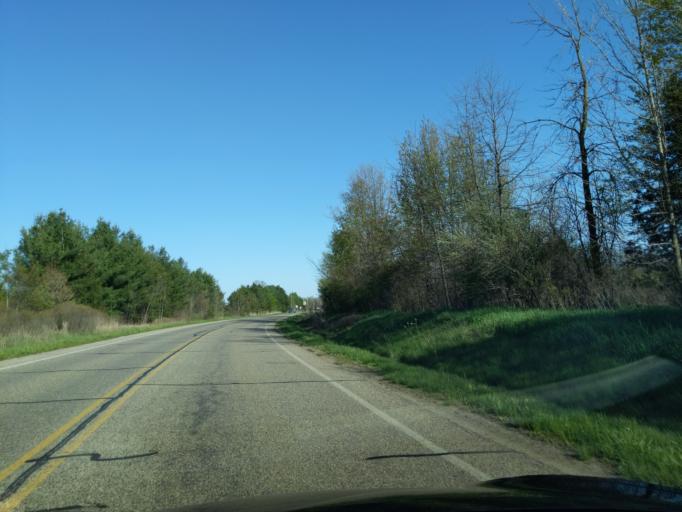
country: US
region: Michigan
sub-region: Ionia County
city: Portland
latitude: 42.8854
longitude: -84.9908
